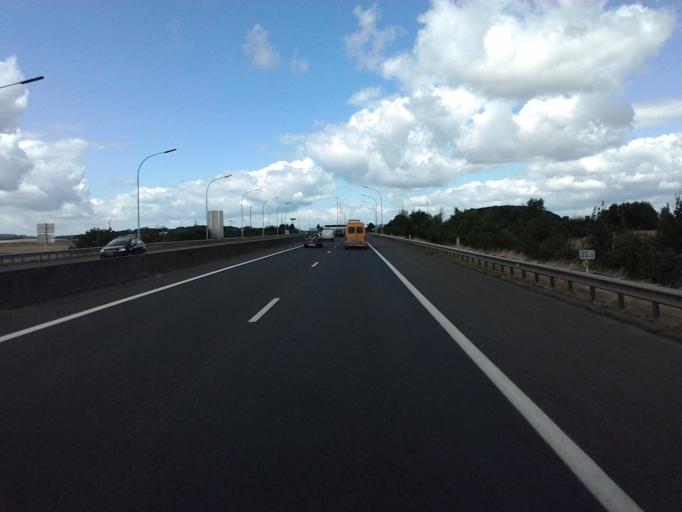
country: LU
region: Luxembourg
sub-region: Canton de Capellen
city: Steinfort
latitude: 49.6380
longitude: 5.9104
